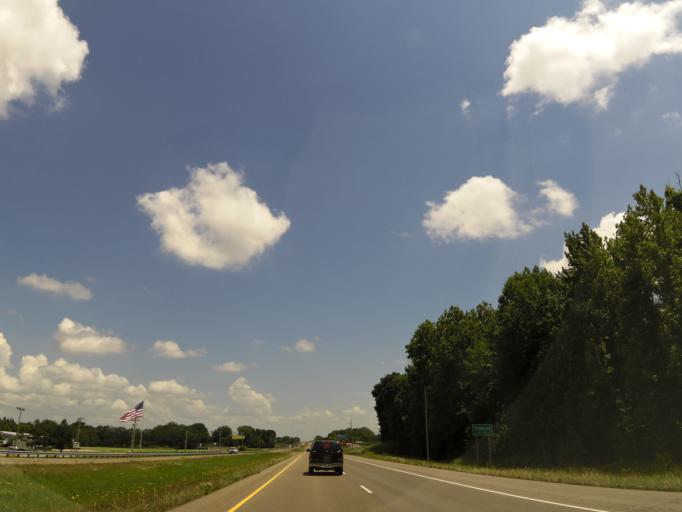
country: US
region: Tennessee
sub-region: Lauderdale County
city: Halls
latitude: 35.9037
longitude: -89.2535
